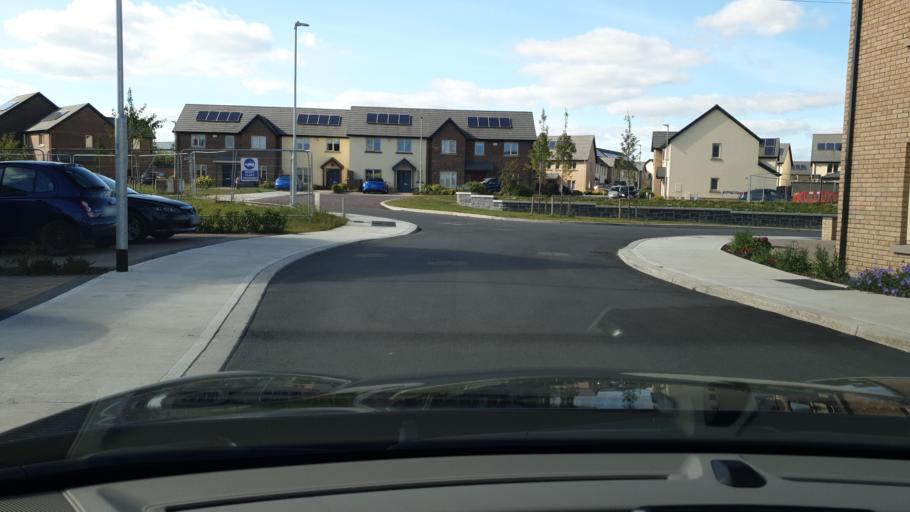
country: IE
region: Leinster
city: Hartstown
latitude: 53.3889
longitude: -6.4432
